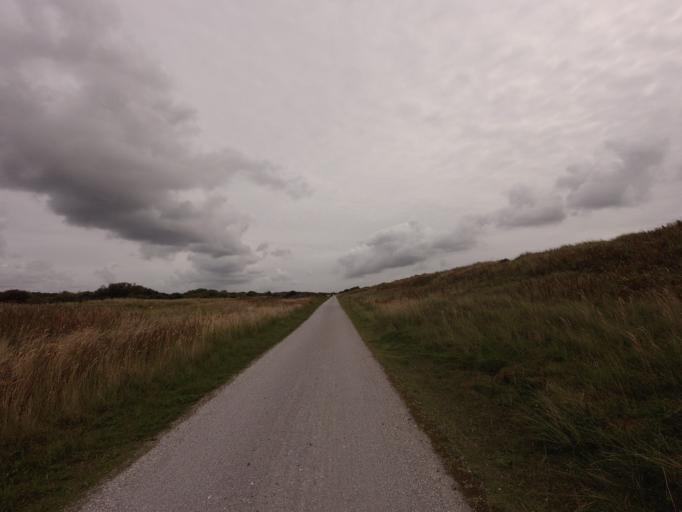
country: NL
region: Friesland
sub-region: Gemeente Ameland
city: Hollum
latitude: 53.4582
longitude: 5.6749
